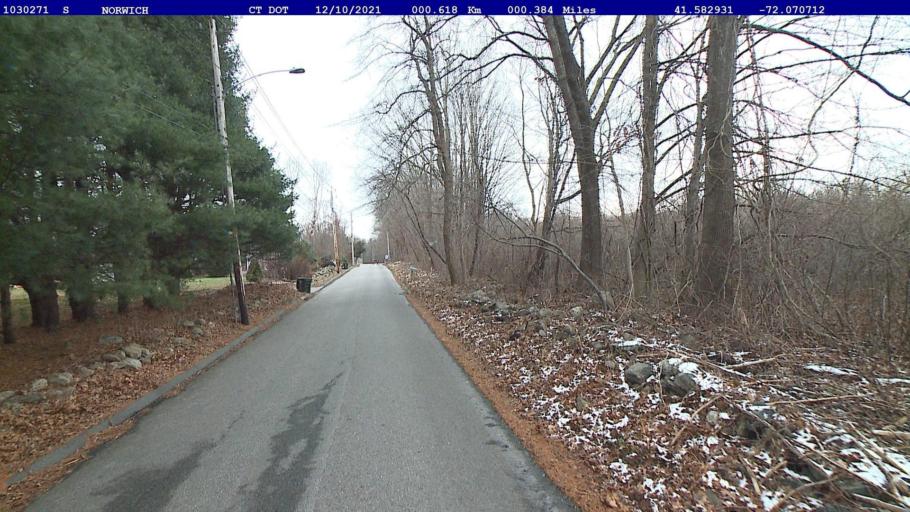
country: US
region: Connecticut
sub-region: New London County
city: Baltic
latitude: 41.5829
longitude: -72.0707
